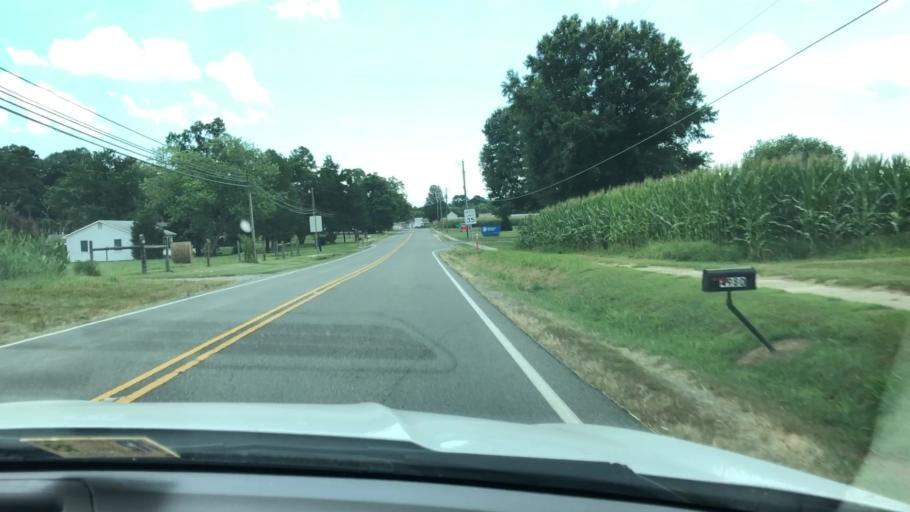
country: US
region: Virginia
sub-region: Lancaster County
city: Lancaster
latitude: 37.7833
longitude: -76.5152
